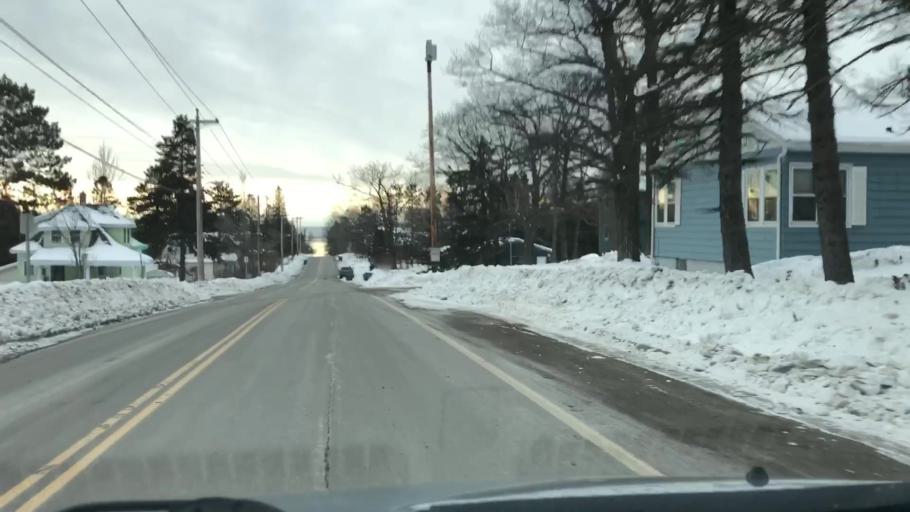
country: US
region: Minnesota
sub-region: Saint Louis County
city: Arnold
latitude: 46.8362
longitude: -92.0639
